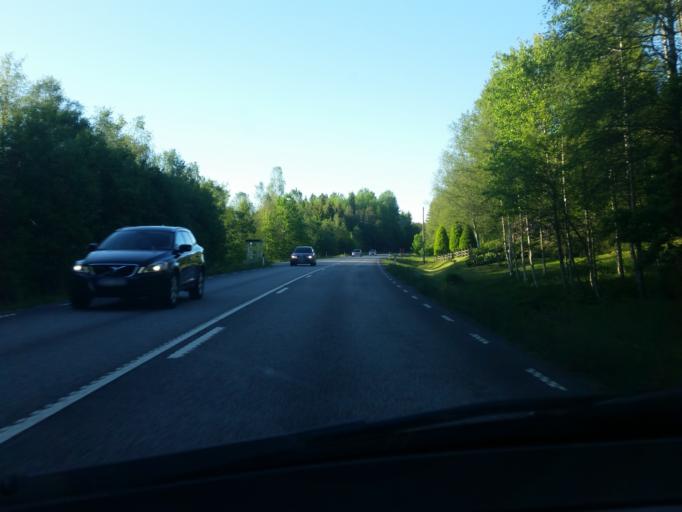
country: SE
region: Vaestra Goetaland
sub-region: Fargelanda Kommun
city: Faergelanda
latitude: 58.5269
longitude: 11.9786
